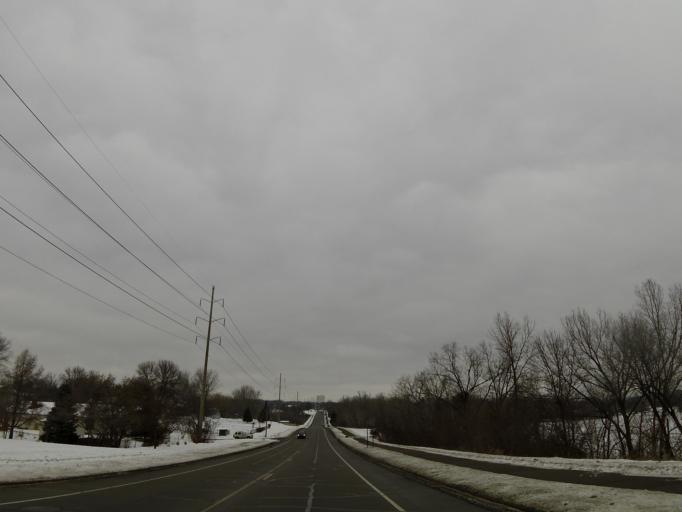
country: US
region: Minnesota
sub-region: Dakota County
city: Burnsville
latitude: 44.7422
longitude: -93.2582
